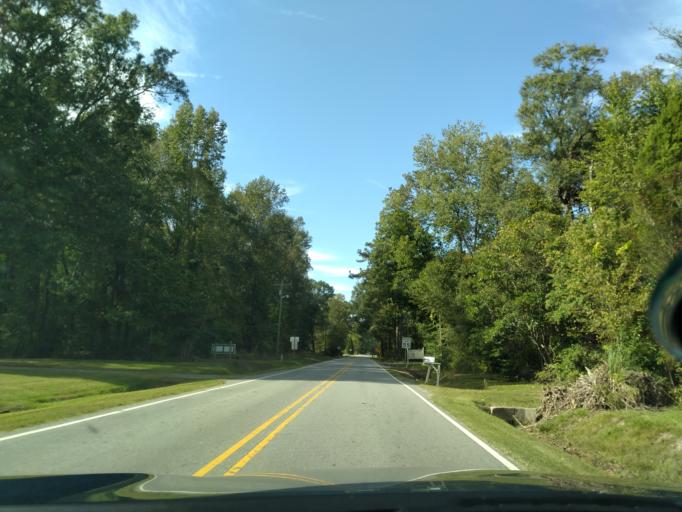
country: US
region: North Carolina
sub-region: Beaufort County
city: Belhaven
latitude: 35.5919
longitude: -76.6644
